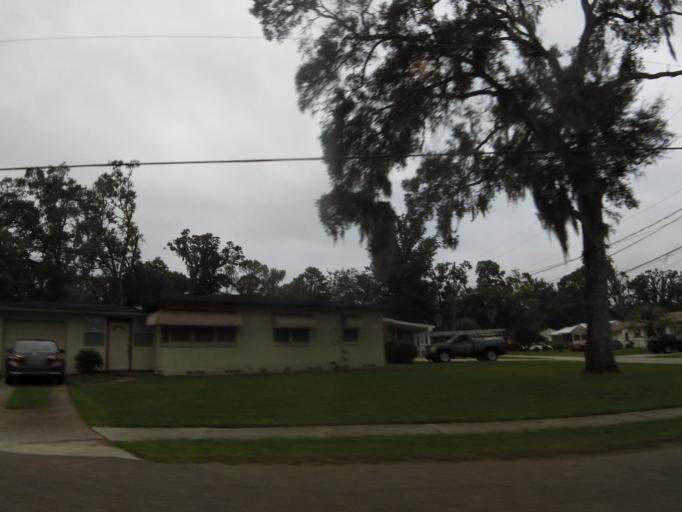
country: US
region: Florida
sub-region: Clay County
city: Bellair-Meadowbrook Terrace
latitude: 30.2724
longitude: -81.7379
